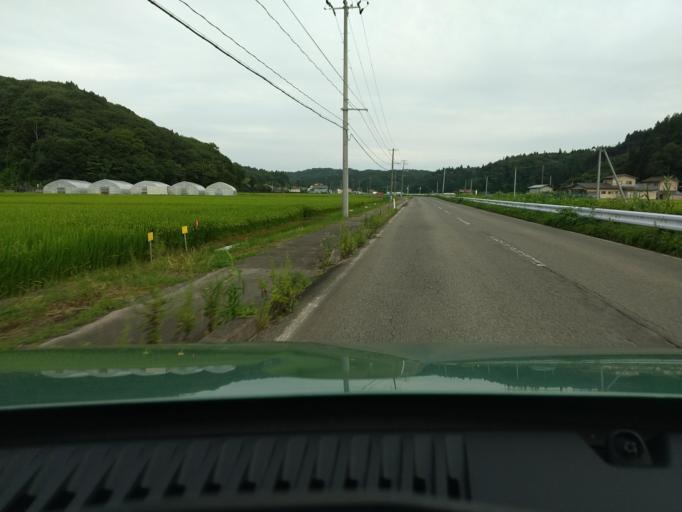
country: JP
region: Akita
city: Akita
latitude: 39.7852
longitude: 140.1238
